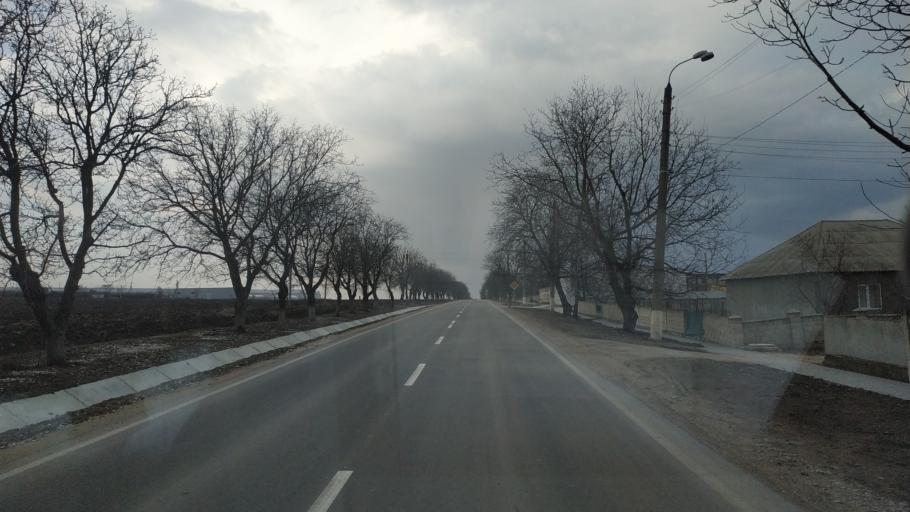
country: MD
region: Telenesti
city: Grigoriopol
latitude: 47.0137
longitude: 29.2889
